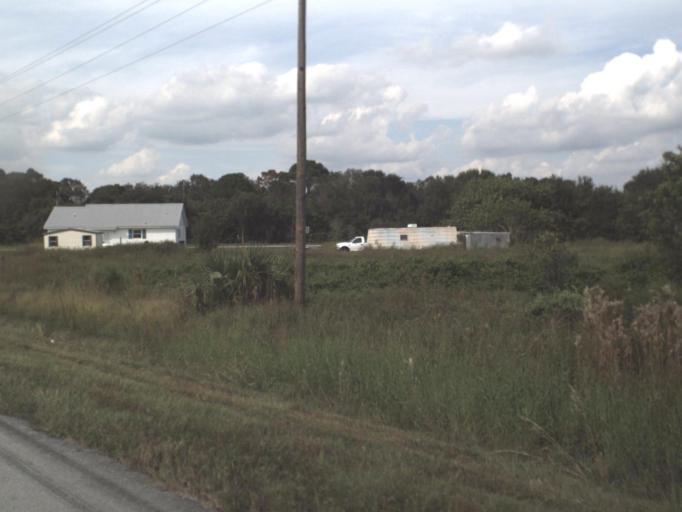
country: US
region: Florida
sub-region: Okeechobee County
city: Taylor Creek
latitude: 27.2174
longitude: -80.7617
